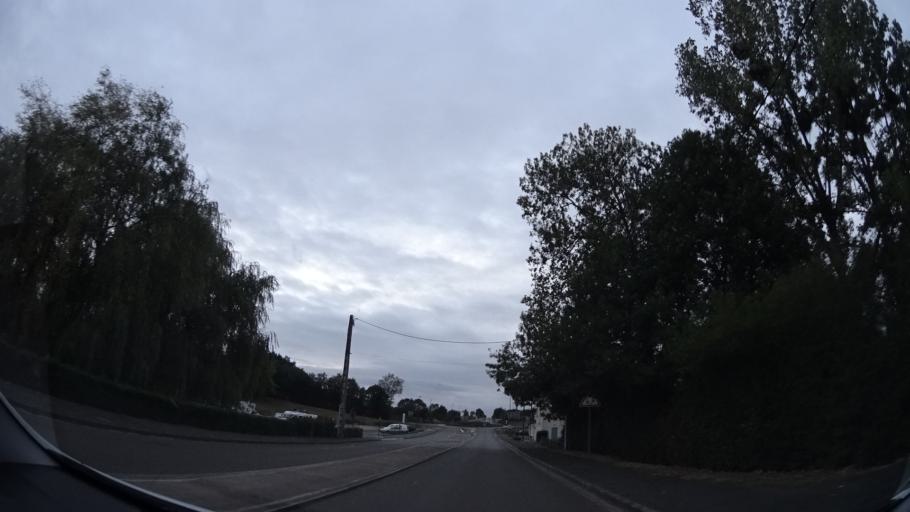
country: FR
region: Pays de la Loire
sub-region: Departement de la Mayenne
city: Vaiges
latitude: 48.0420
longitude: -0.4820
